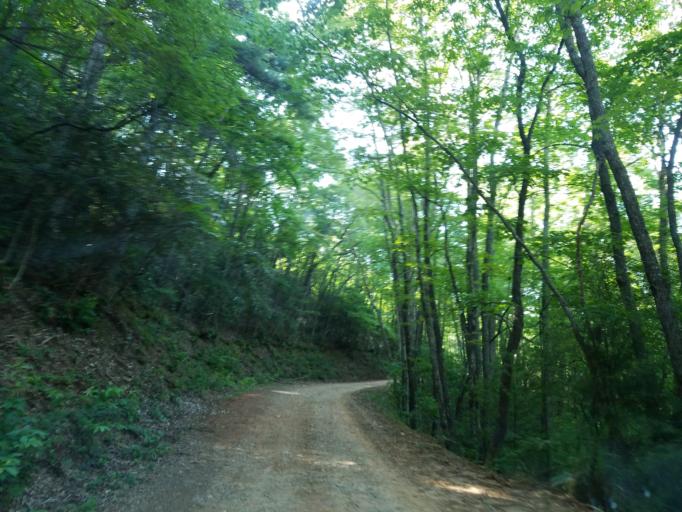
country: US
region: Georgia
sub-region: Dawson County
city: Dawsonville
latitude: 34.5869
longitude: -84.2026
